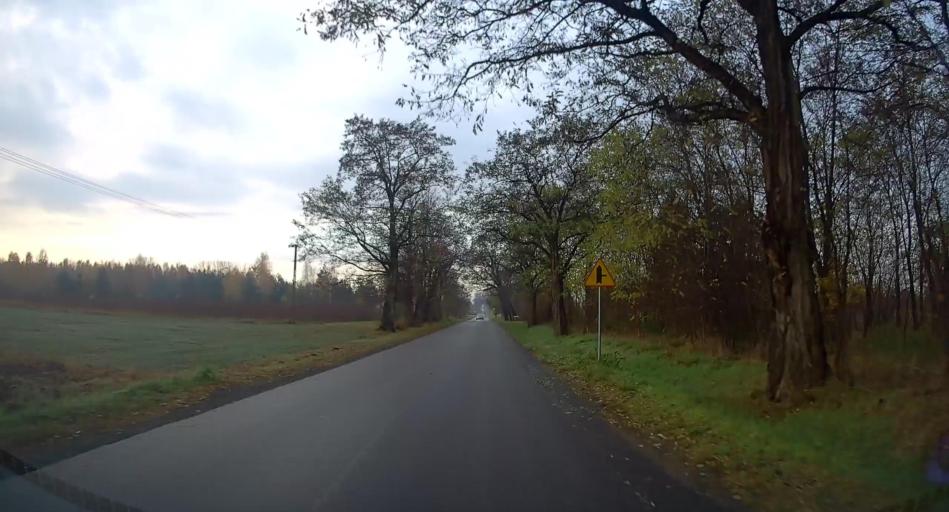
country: PL
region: Masovian Voivodeship
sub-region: Powiat zyrardowski
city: Puszcza Marianska
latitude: 51.9307
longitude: 20.3616
